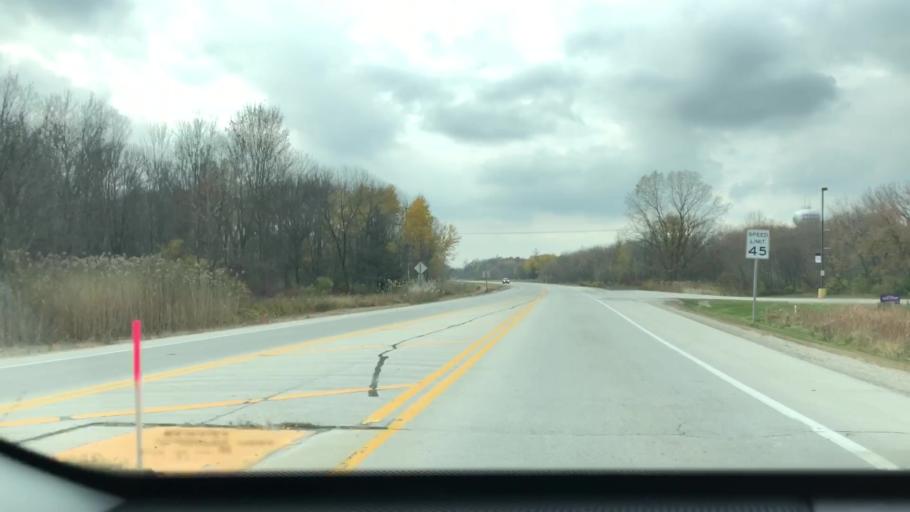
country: US
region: Wisconsin
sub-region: Brown County
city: Oneida
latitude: 44.5015
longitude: -88.1957
